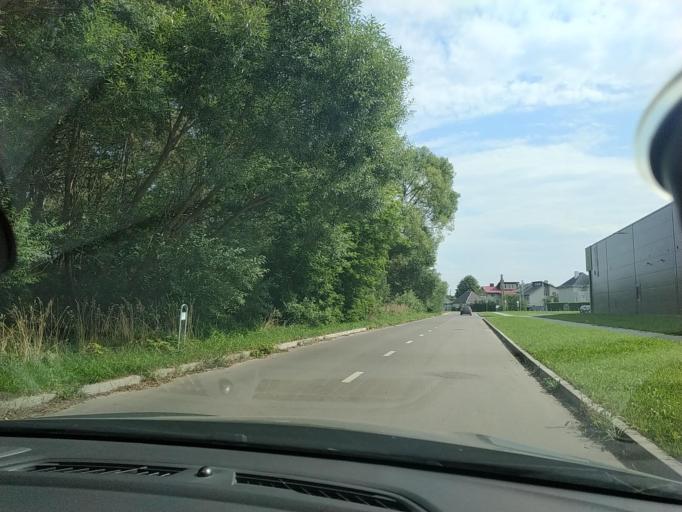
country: LT
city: Nemencine
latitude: 54.8454
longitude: 25.4595
